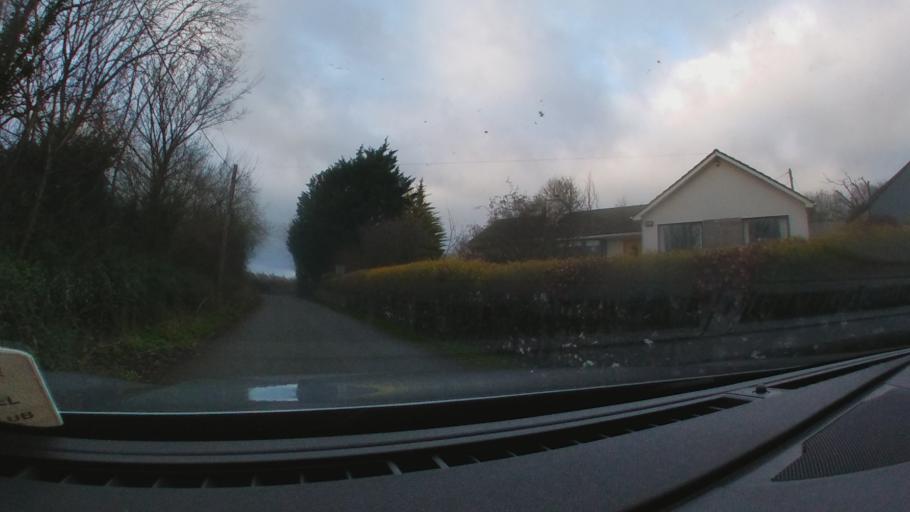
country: IE
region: Leinster
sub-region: Kilkenny
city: Thomastown
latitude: 52.5882
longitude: -7.1745
